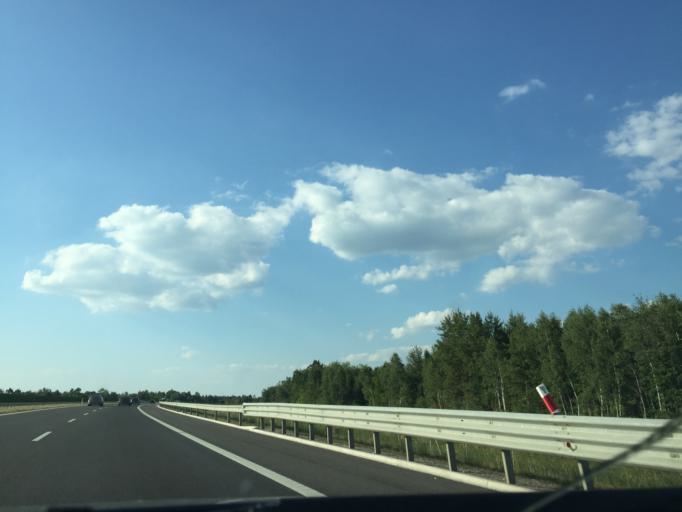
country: PL
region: Swietokrzyskie
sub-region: Powiat skarzyski
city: Skarzysko-Kamienna
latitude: 51.1331
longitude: 20.8343
